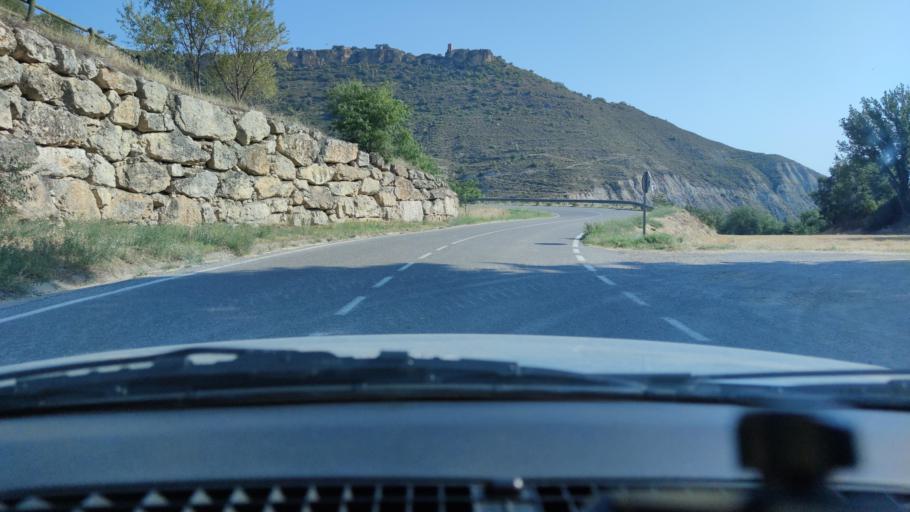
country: ES
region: Catalonia
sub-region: Provincia de Lleida
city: Llimiana
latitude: 42.0943
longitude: 0.8756
